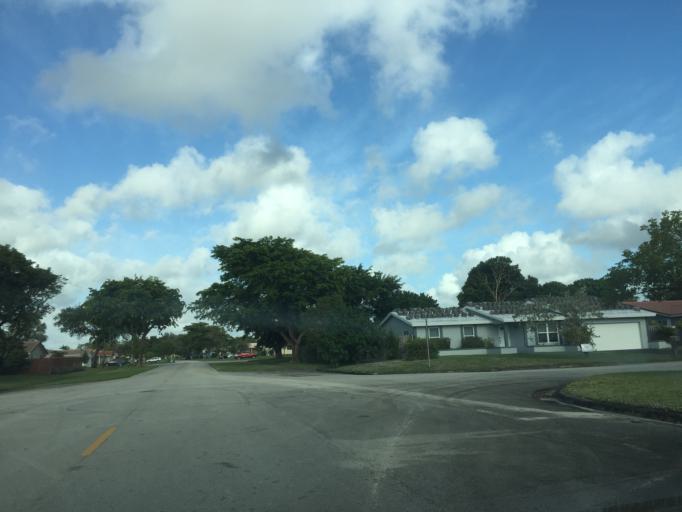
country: US
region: Florida
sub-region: Broward County
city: North Lauderdale
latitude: 26.2444
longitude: -80.2380
